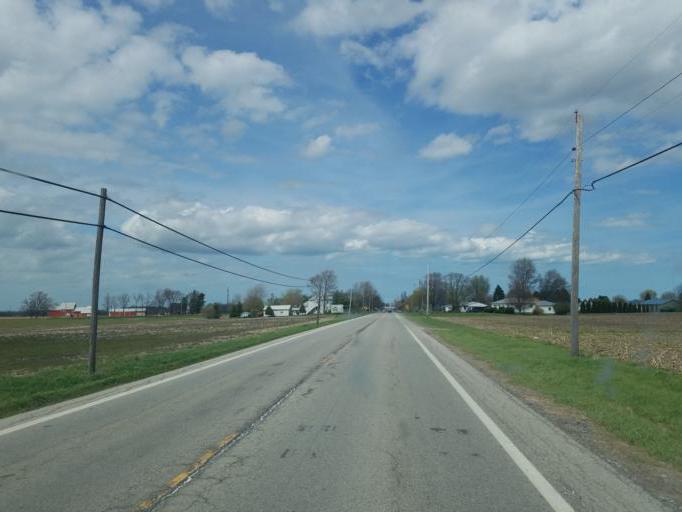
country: US
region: Ohio
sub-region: Erie County
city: Sandusky
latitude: 41.3932
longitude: -82.7340
